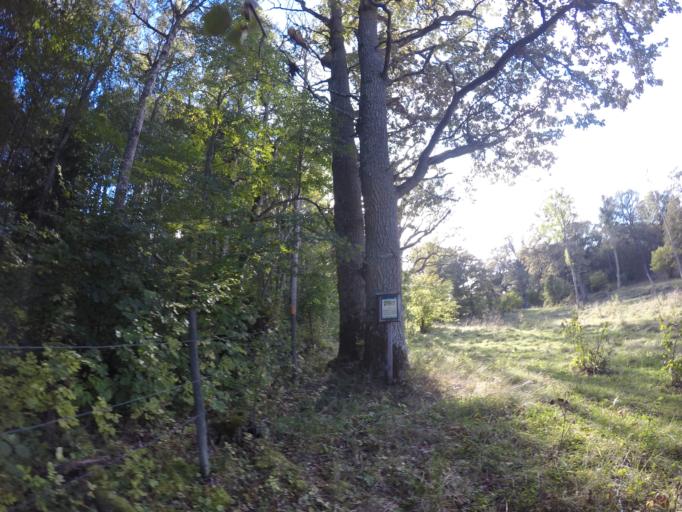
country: SE
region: Vaestmanland
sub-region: Hallstahammars Kommun
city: Kolback
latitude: 59.4799
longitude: 16.2275
